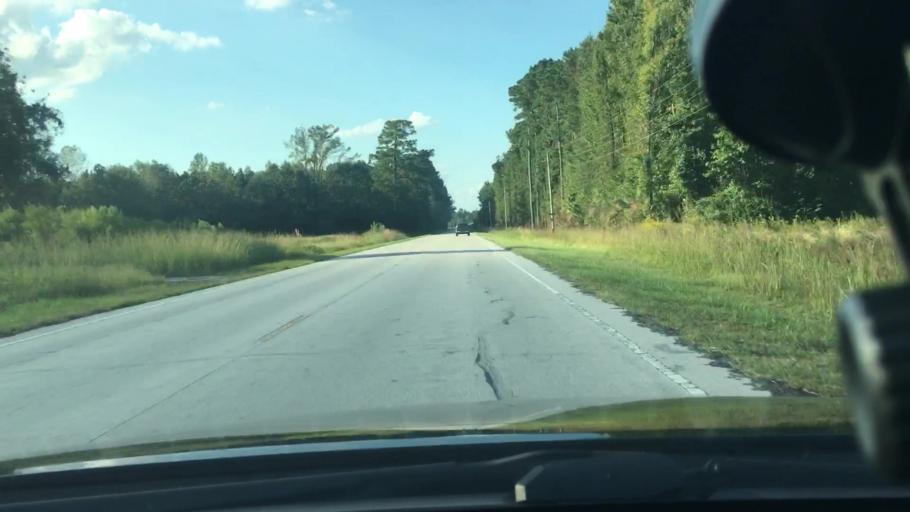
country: US
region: North Carolina
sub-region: Craven County
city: Vanceboro
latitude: 35.3943
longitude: -77.2333
